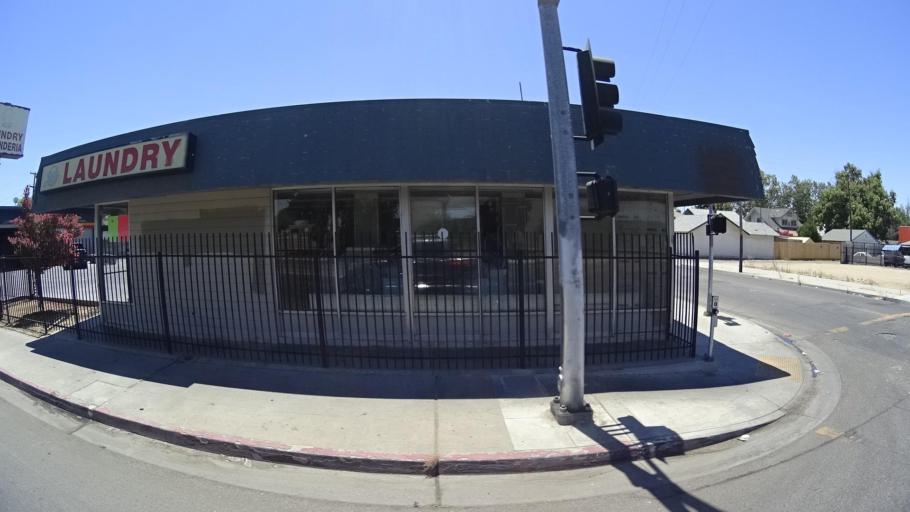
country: US
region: California
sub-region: Fresno County
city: Fresno
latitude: 36.7504
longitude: -119.7791
